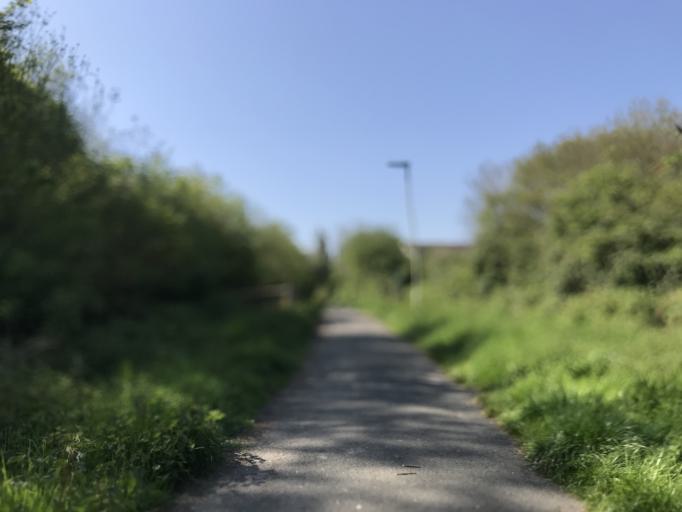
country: GB
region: England
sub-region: Devon
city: Barnstaple
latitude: 51.0722
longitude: -4.0423
